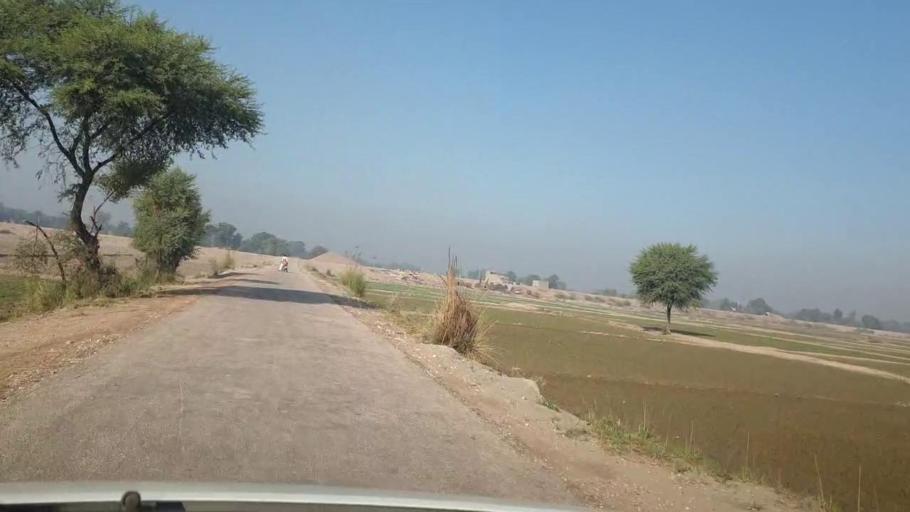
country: PK
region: Sindh
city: Dadu
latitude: 26.6778
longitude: 67.8138
